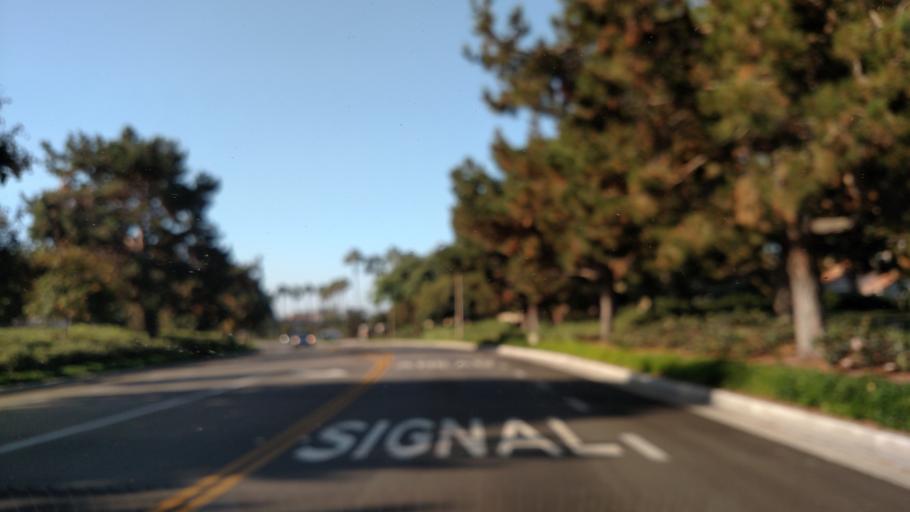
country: US
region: California
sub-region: Orange County
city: Irvine
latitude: 33.6800
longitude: -117.8197
